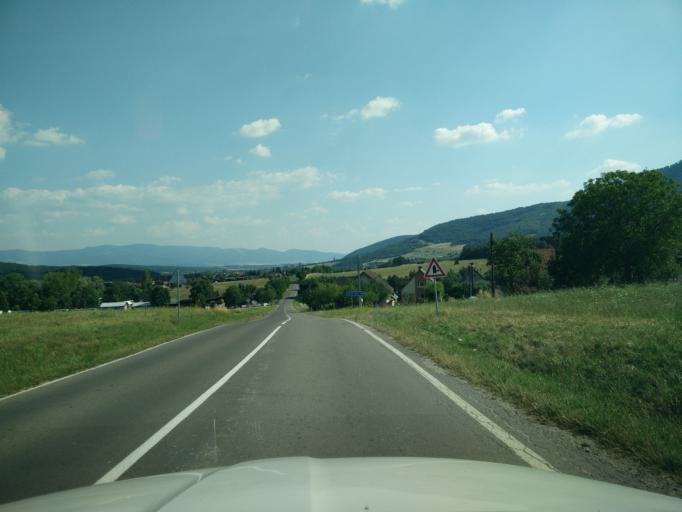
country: SK
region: Nitriansky
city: Novaky
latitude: 48.8068
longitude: 18.4746
